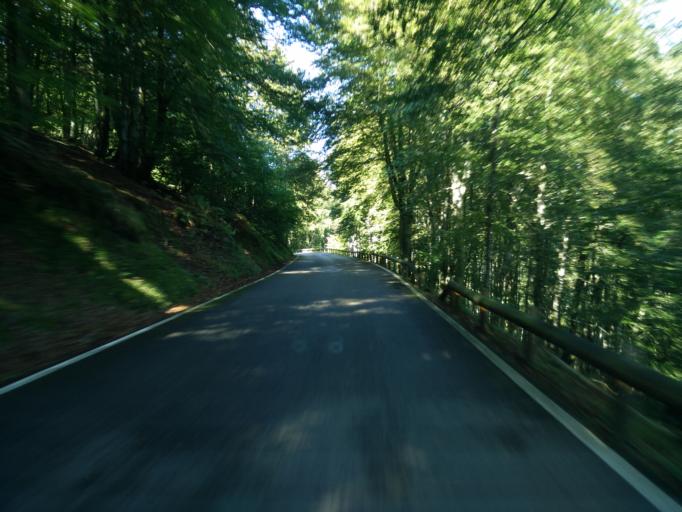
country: ES
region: Cantabria
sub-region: Provincia de Cantabria
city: Ruente
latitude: 43.0990
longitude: -4.2666
